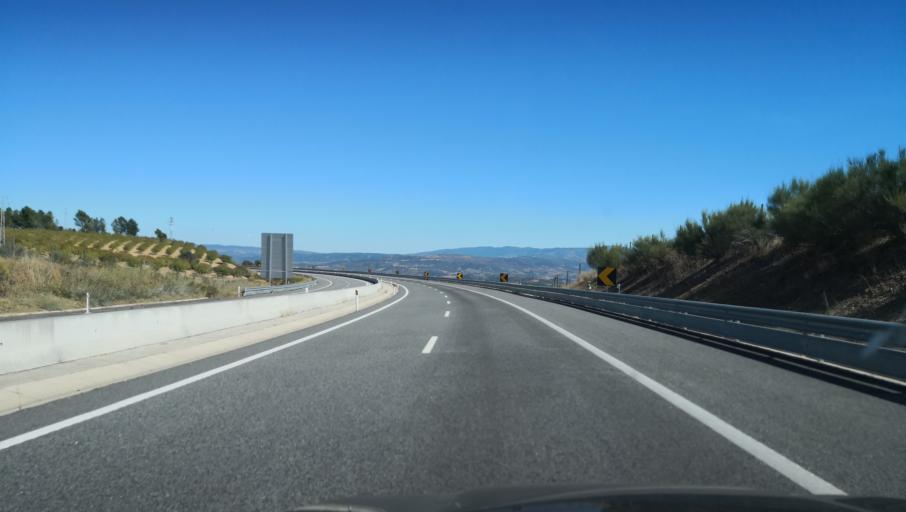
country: PT
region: Braganca
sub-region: Mirandela
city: Mirandela
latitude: 41.4509
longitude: -7.2735
